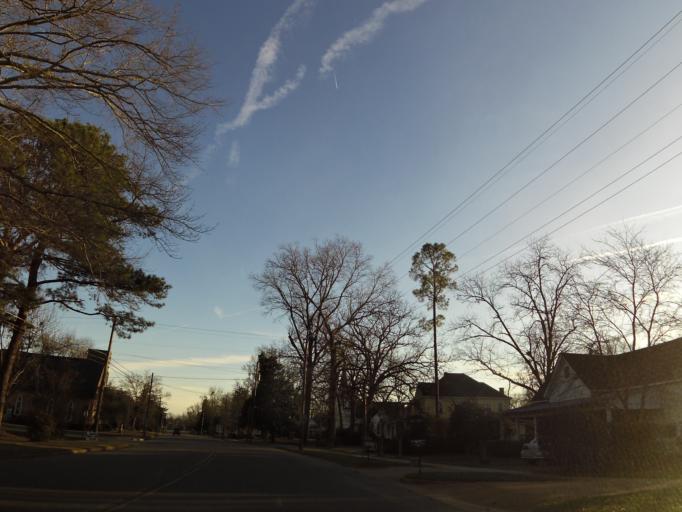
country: US
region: Georgia
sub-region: Webster County
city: Preston
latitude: 32.0381
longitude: -84.3939
